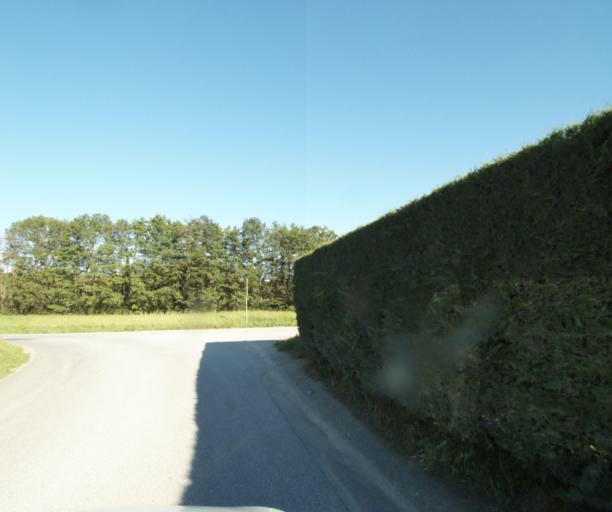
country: FR
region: Rhone-Alpes
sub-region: Departement de la Haute-Savoie
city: Loisin
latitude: 46.2938
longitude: 6.3016
